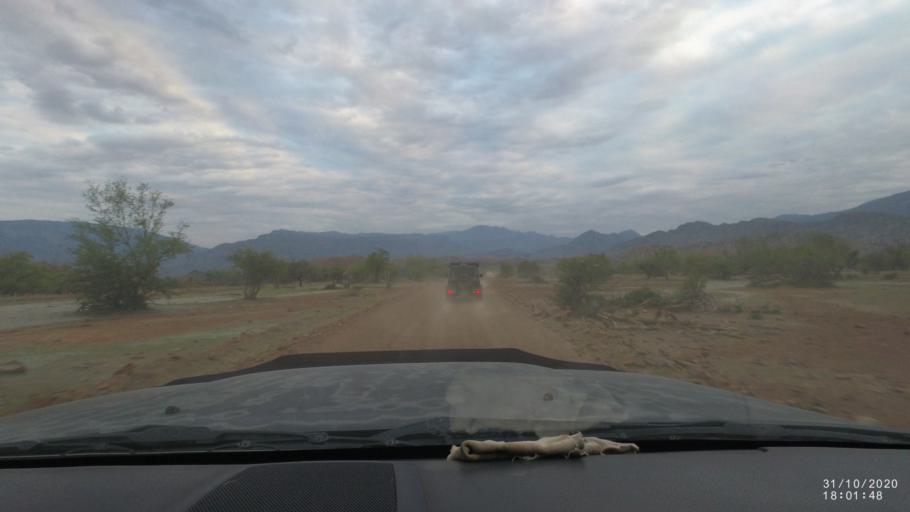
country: BO
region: Chuquisaca
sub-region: Provincia Zudanez
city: Mojocoya
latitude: -18.6644
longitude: -64.5297
